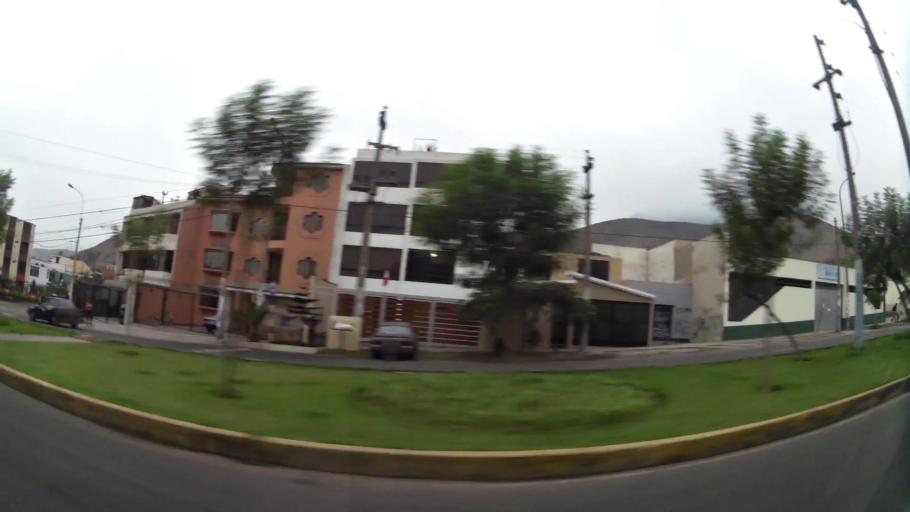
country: PE
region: Lima
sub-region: Lima
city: La Molina
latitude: -12.1079
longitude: -76.9397
